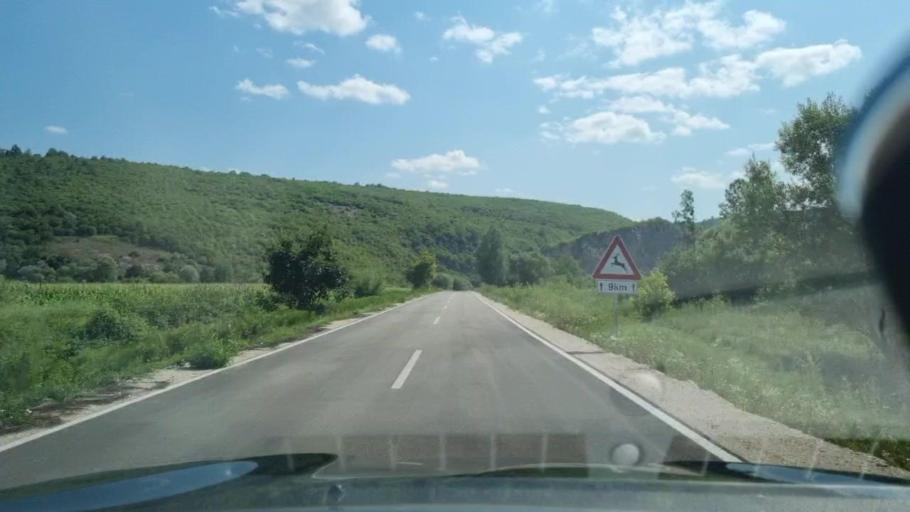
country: BA
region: Federation of Bosnia and Herzegovina
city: Kljuc
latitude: 44.5549
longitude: 16.7994
